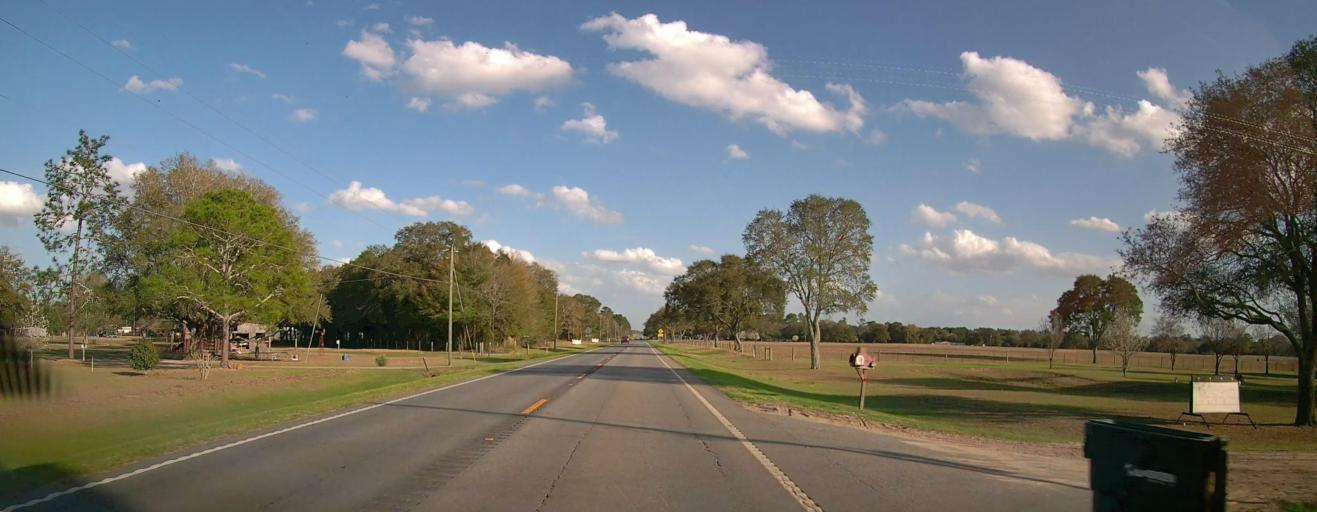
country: US
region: Georgia
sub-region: Tattnall County
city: Reidsville
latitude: 32.1126
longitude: -82.1811
